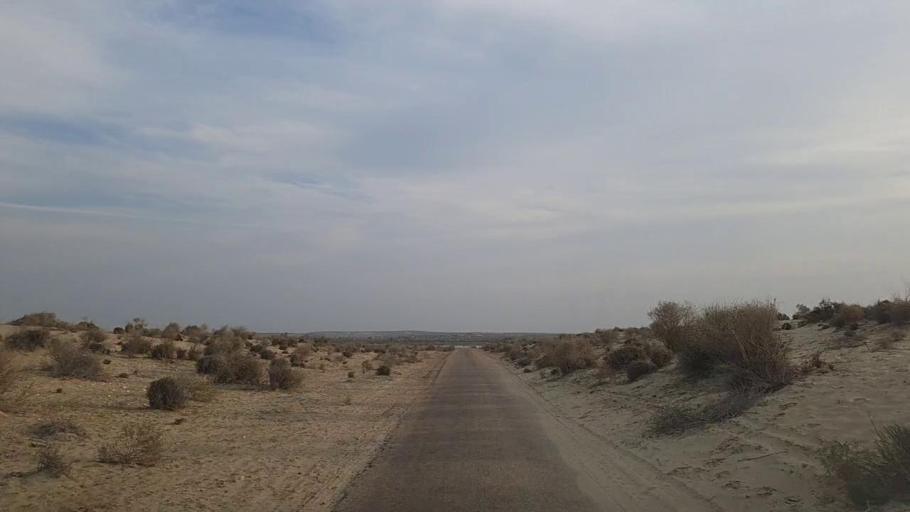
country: PK
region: Sindh
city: Daur
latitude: 26.5002
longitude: 68.5209
